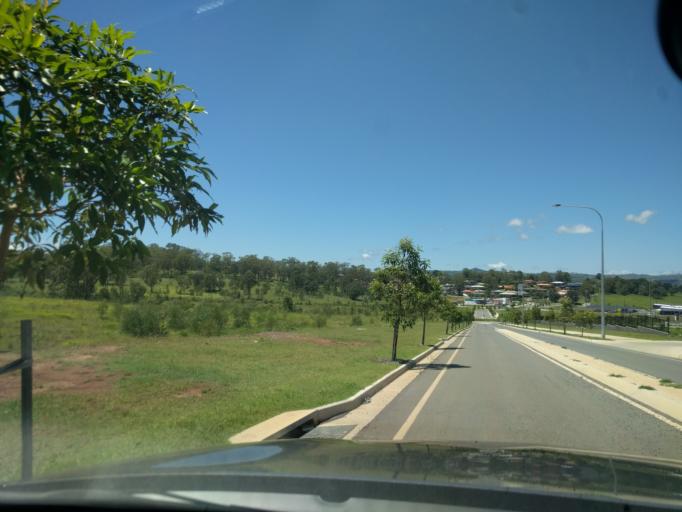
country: AU
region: Queensland
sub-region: Logan
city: Cedar Vale
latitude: -27.9889
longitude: 153.0129
